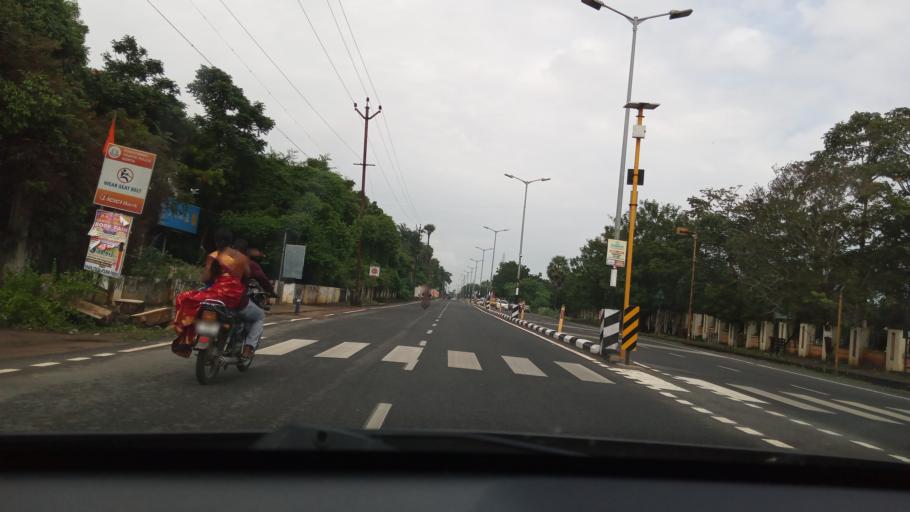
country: IN
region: Tamil Nadu
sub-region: Villupuram
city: Auroville
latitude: 12.0123
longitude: 79.8574
